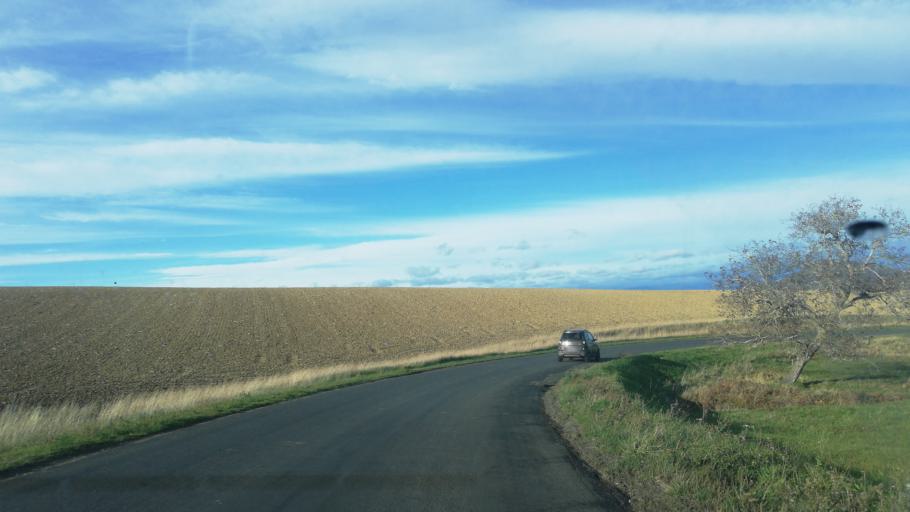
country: FR
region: Auvergne
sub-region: Departement du Puy-de-Dome
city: Billom
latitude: 45.7039
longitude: 3.3524
